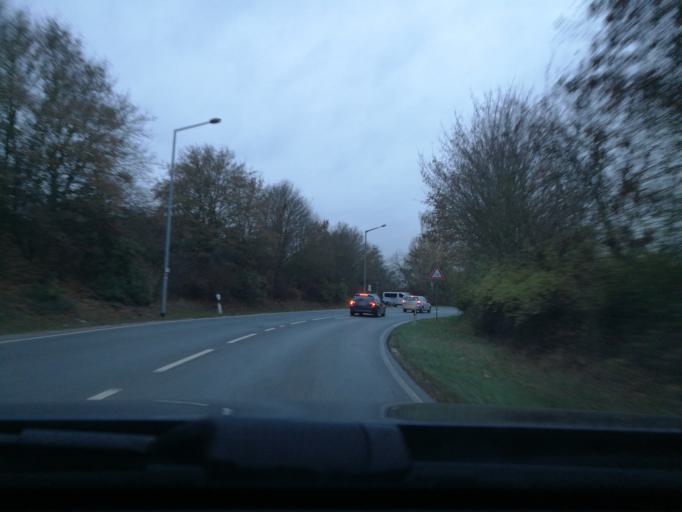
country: DE
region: Bavaria
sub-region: Regierungsbezirk Mittelfranken
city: Furth
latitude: 49.4696
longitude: 10.9631
